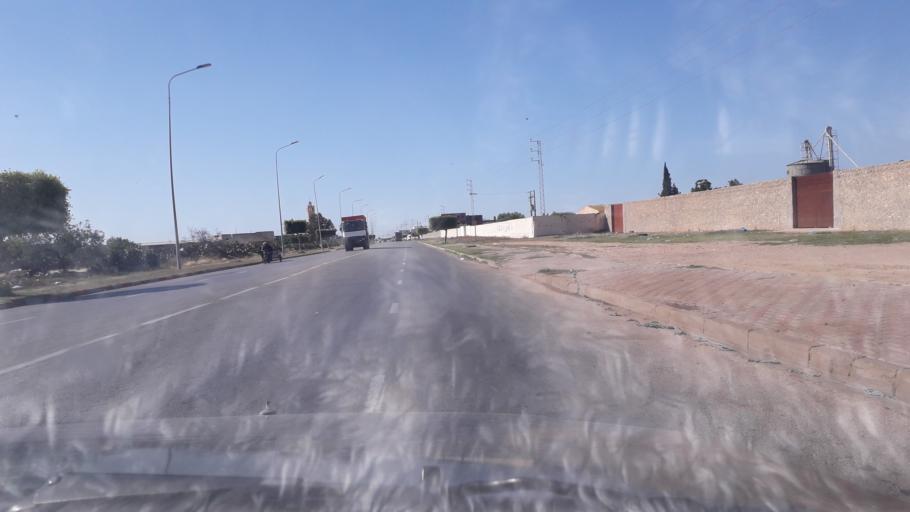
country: TN
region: Safaqis
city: Al Qarmadah
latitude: 34.8536
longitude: 10.7608
